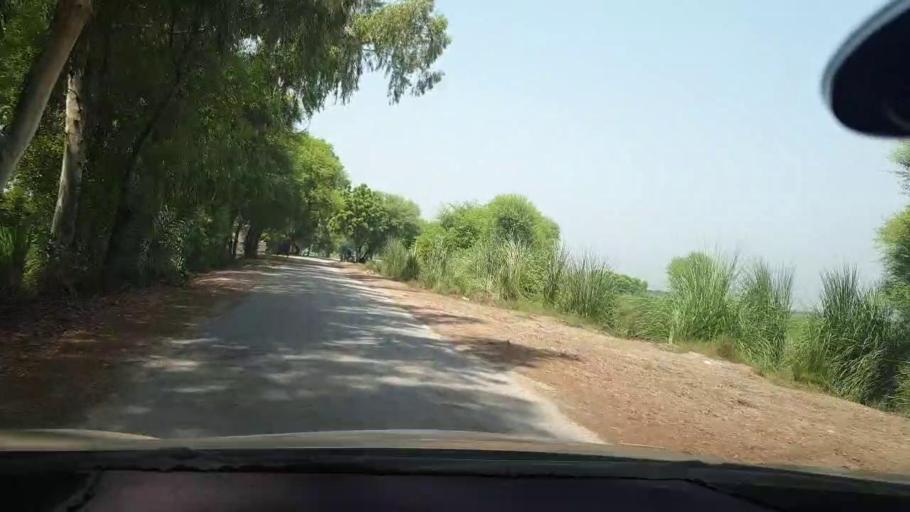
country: PK
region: Sindh
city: Kambar
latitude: 27.6607
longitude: 67.9486
